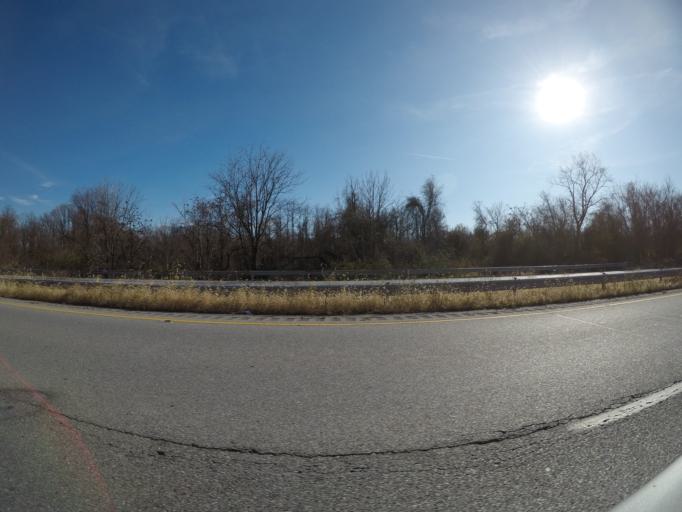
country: US
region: Pennsylvania
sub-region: Chester County
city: Coatesville
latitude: 39.9924
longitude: -75.8590
